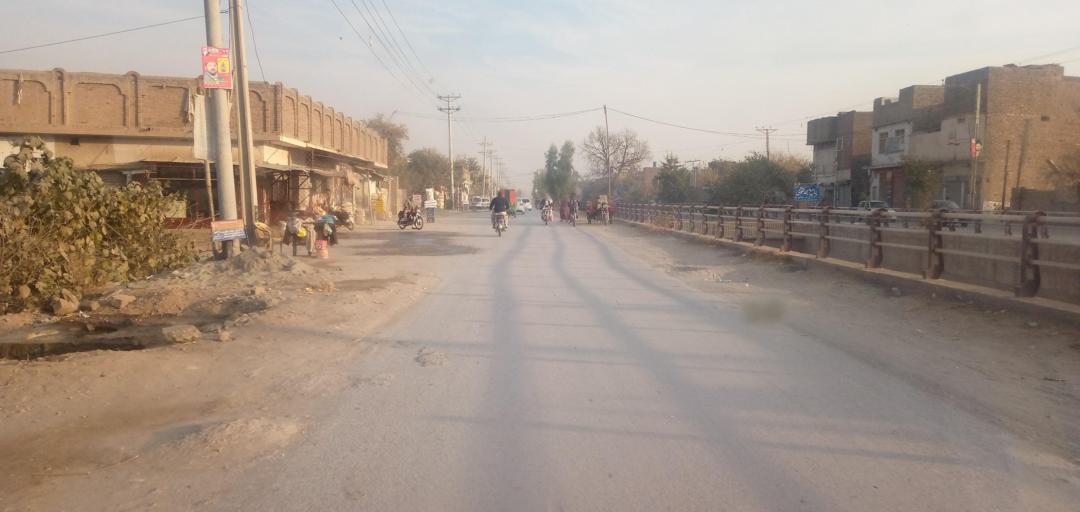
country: PK
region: Khyber Pakhtunkhwa
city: Peshawar
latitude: 33.9728
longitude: 71.5309
